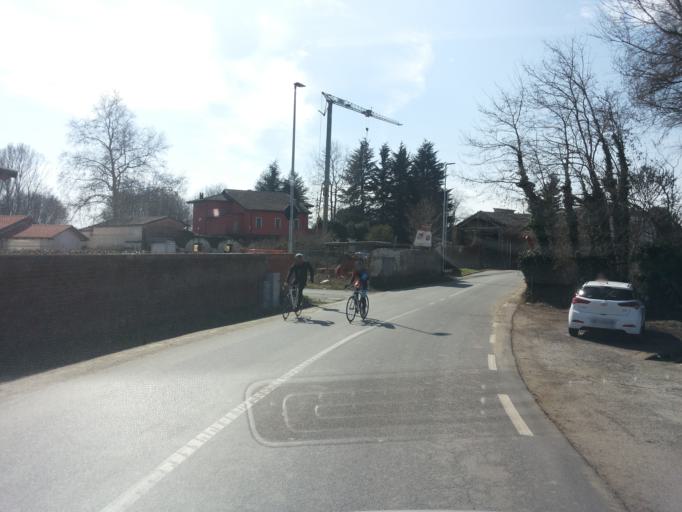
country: IT
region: Piedmont
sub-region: Provincia di Vercelli
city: Asigliano Vercellese
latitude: 45.2600
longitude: 8.4029
